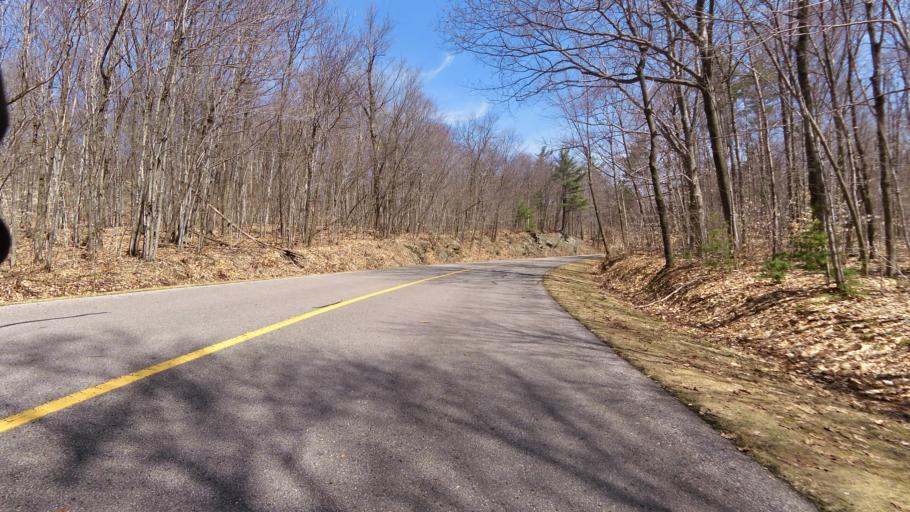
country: CA
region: Quebec
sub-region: Outaouais
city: Gatineau
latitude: 45.4914
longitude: -75.8546
